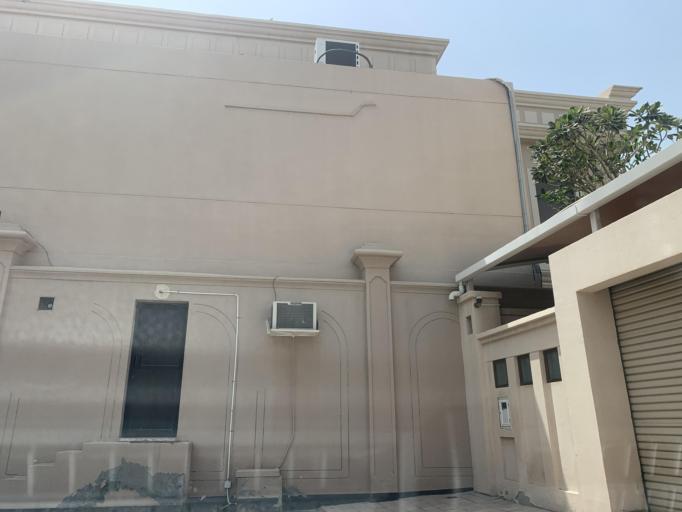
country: BH
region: Northern
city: Madinat `Isa
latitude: 26.1561
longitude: 50.5547
